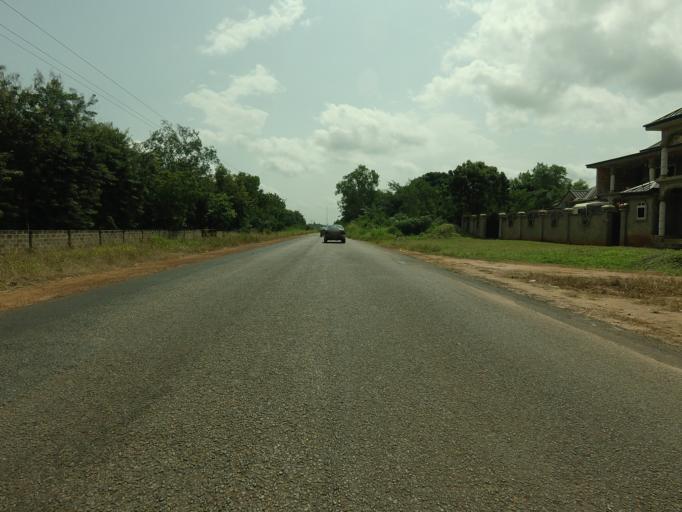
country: TG
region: Maritime
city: Lome
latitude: 6.2277
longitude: 1.0168
